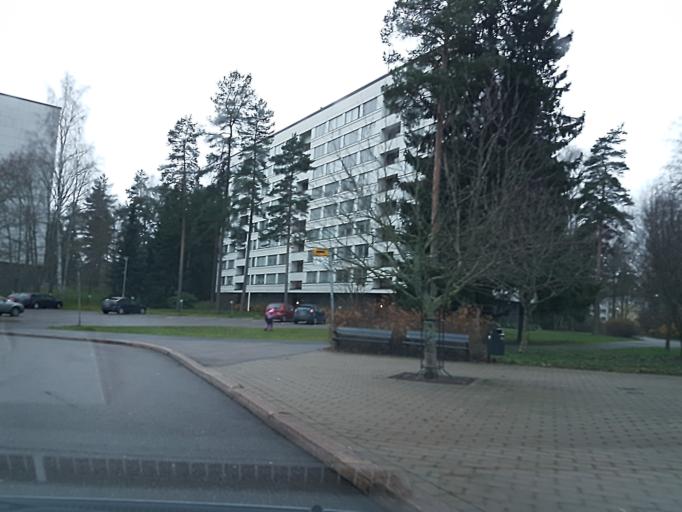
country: FI
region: Uusimaa
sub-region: Helsinki
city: Vantaa
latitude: 60.2348
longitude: 25.0869
